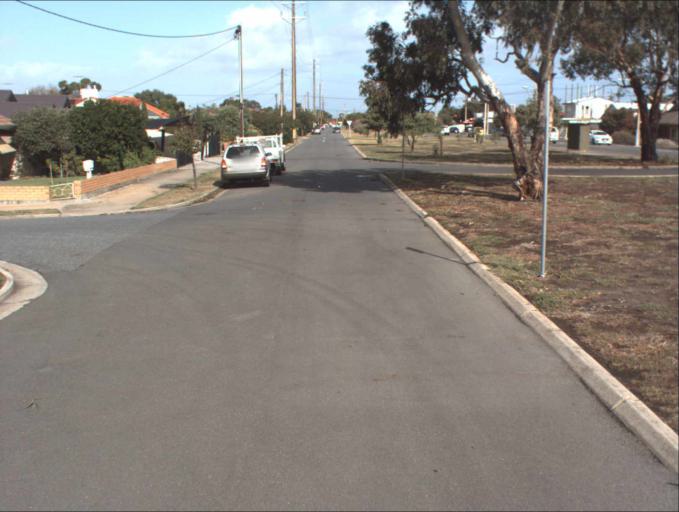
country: AU
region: South Australia
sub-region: Port Adelaide Enfield
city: Birkenhead
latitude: -34.8129
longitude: 138.4947
